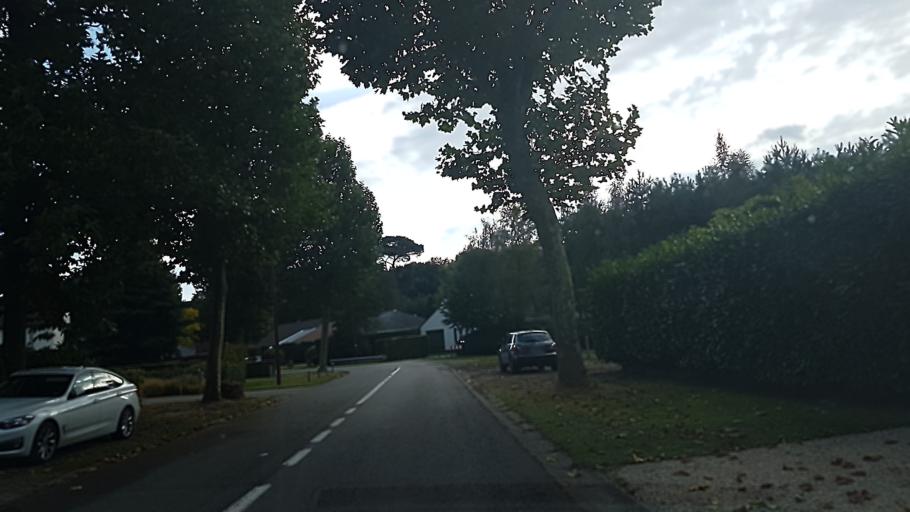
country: BE
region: Flanders
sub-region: Provincie Antwerpen
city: Stabroek
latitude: 51.3496
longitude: 4.3896
